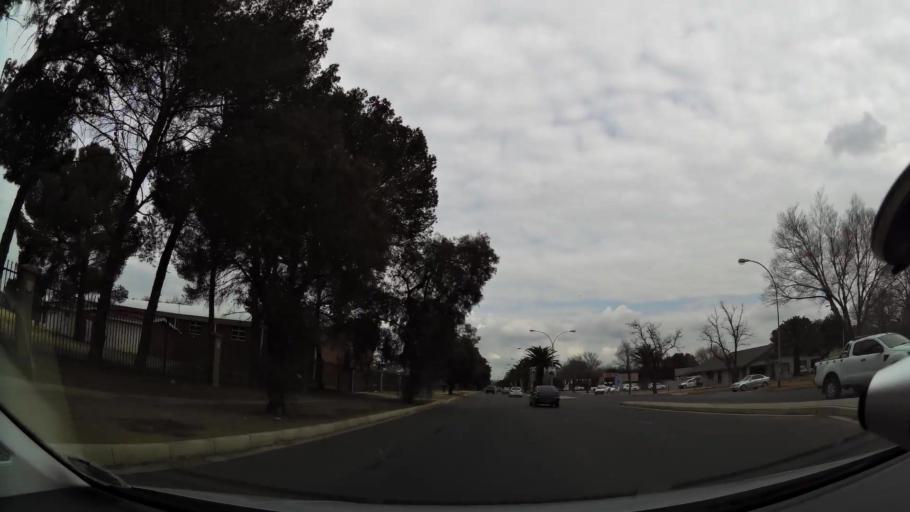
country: ZA
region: Orange Free State
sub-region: Mangaung Metropolitan Municipality
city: Bloemfontein
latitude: -29.1032
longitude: 26.2040
